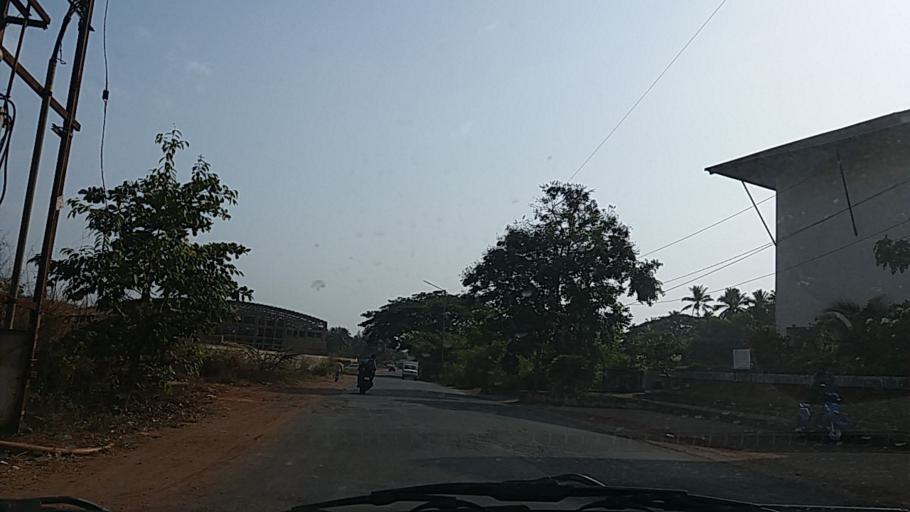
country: IN
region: Goa
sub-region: South Goa
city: Madgaon
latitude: 15.2591
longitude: 73.9680
